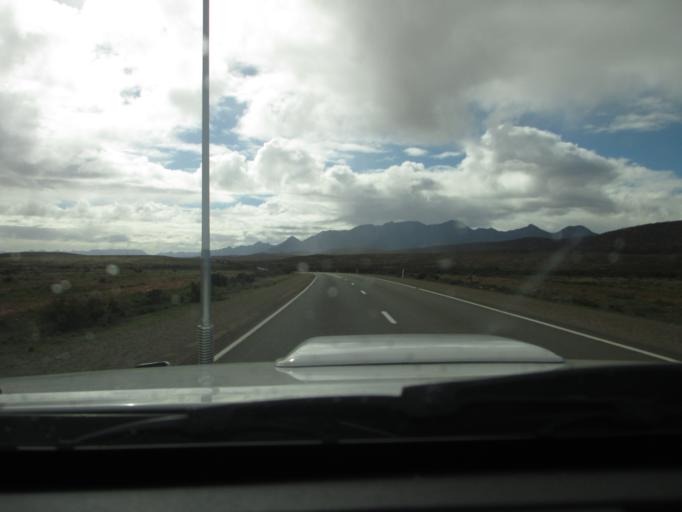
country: AU
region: South Australia
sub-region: Flinders Ranges
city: Quorn
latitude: -31.5926
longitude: 138.4114
